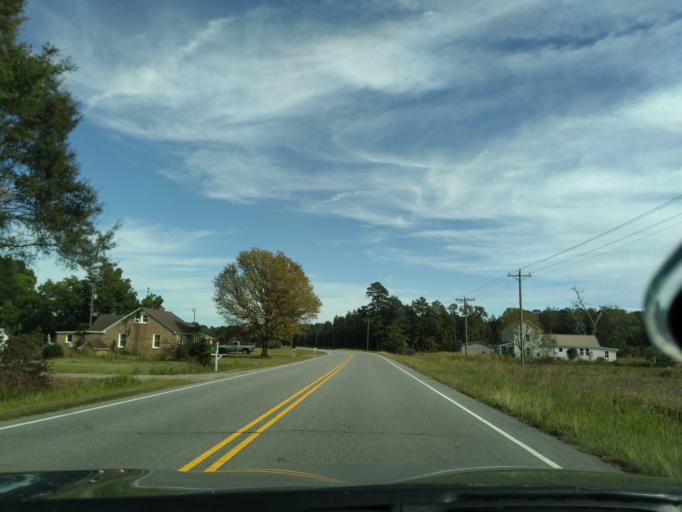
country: US
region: North Carolina
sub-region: Beaufort County
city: River Road
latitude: 35.5213
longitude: -76.8249
